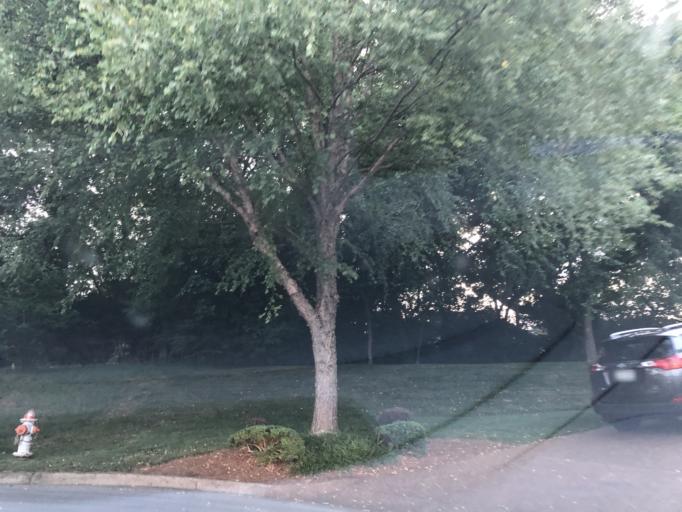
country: US
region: Tennessee
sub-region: Cheatham County
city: Pegram
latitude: 36.0491
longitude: -86.9582
